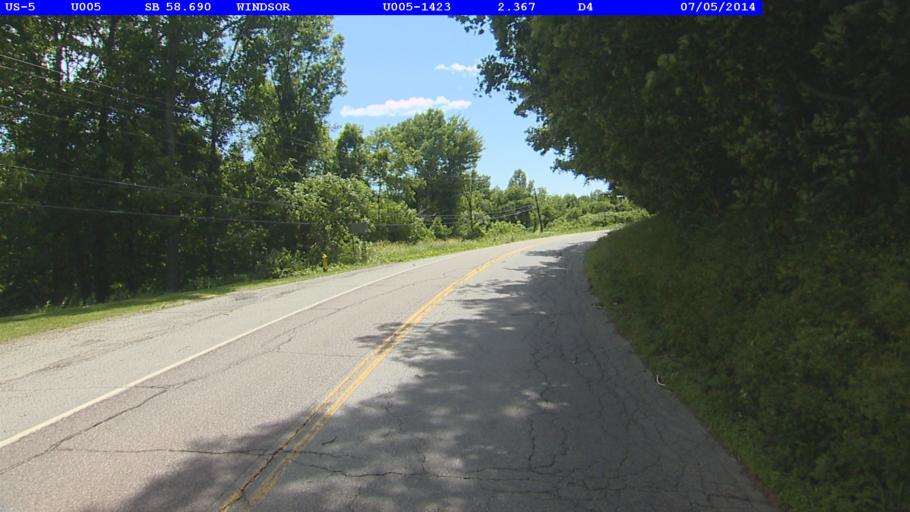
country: US
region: Vermont
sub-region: Windsor County
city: Windsor
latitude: 43.4622
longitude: -72.3932
